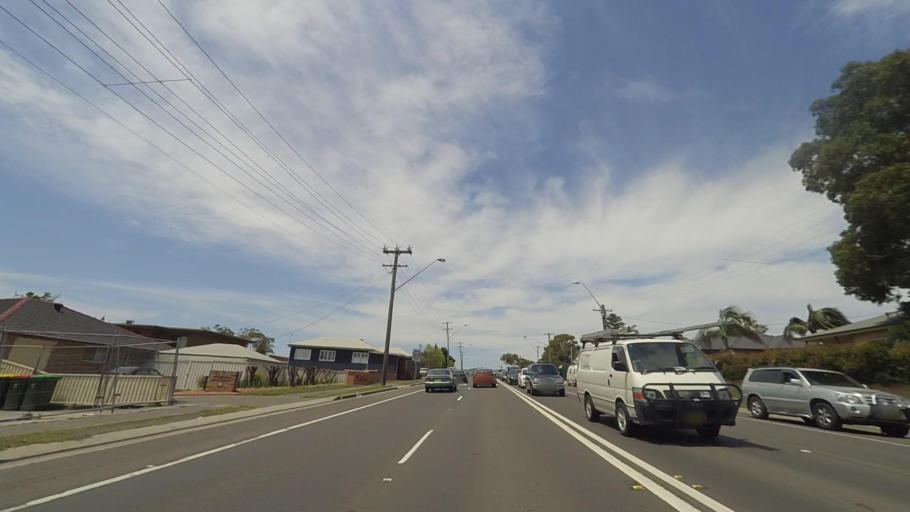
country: AU
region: New South Wales
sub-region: Shellharbour
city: Albion Park Rail
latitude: -34.5649
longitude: 150.7994
